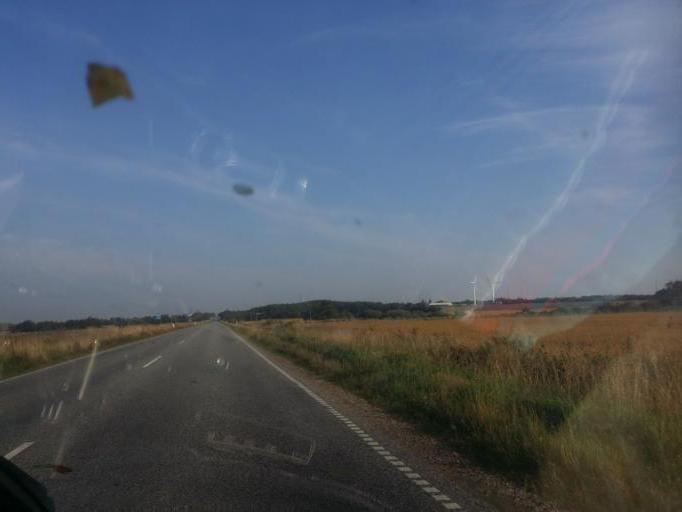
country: DK
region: South Denmark
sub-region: Tonder Kommune
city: Sherrebek
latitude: 55.1413
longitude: 8.7918
